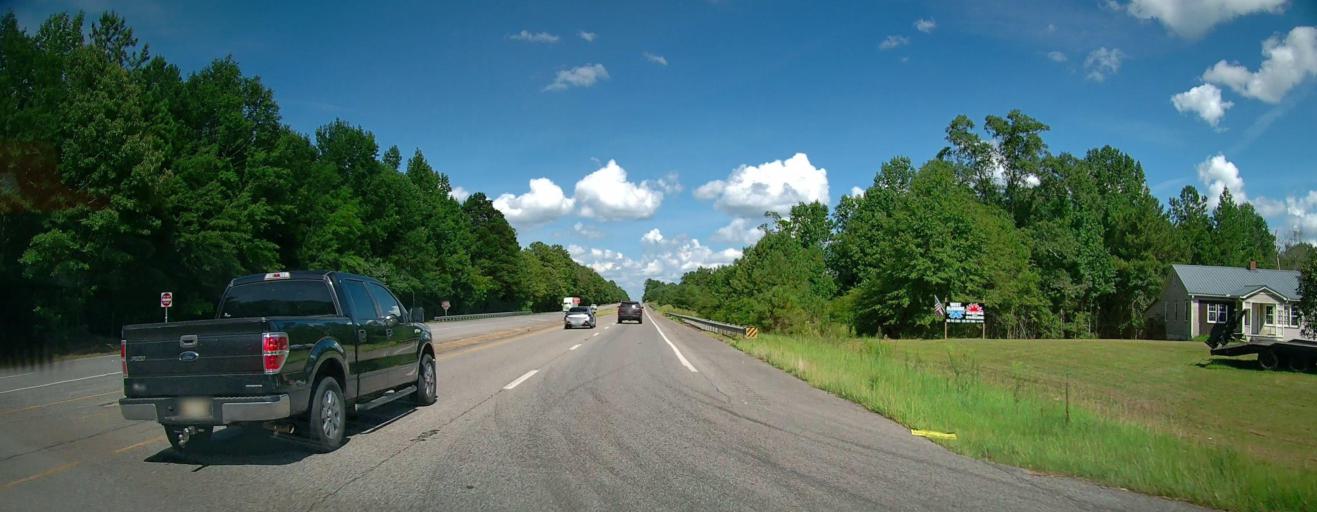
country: US
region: Alabama
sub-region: Pickens County
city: Gordo
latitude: 33.2829
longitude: -87.8224
